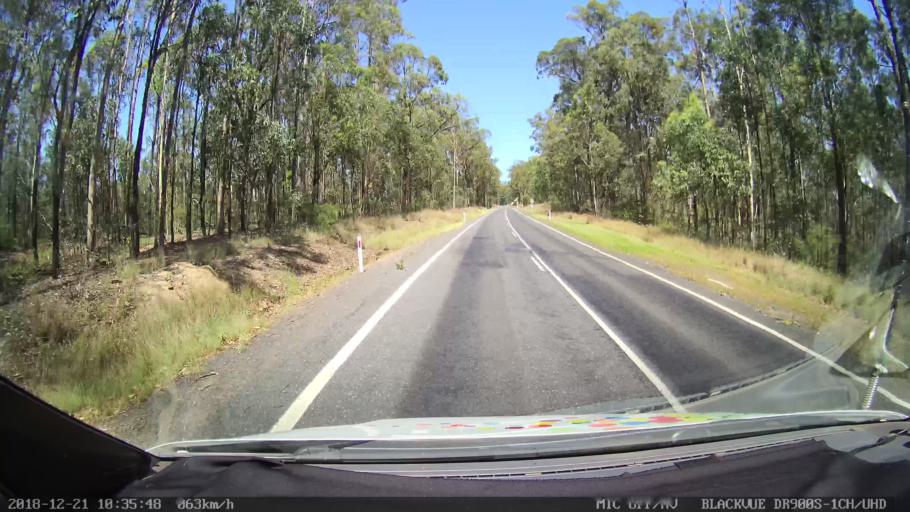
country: AU
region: New South Wales
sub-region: Clarence Valley
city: South Grafton
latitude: -29.6214
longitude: 152.6410
